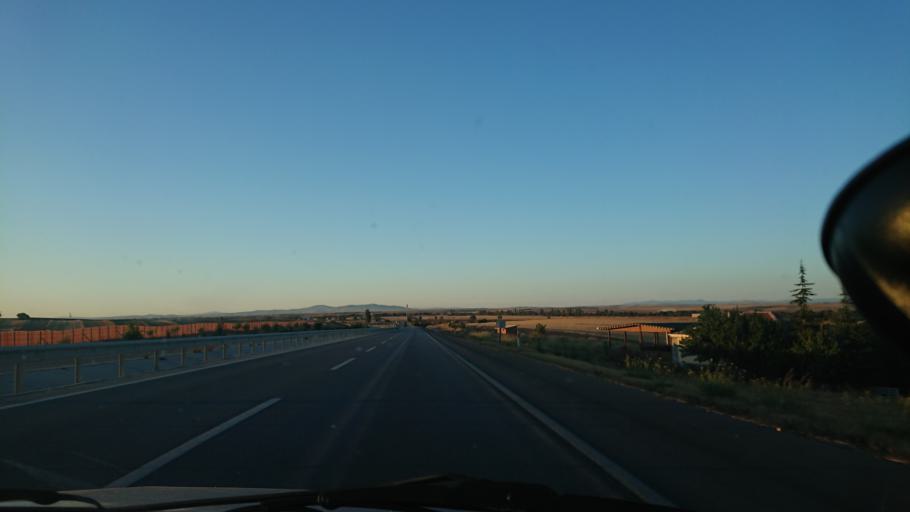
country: TR
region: Eskisehir
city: Mahmudiye
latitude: 39.5124
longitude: 30.9642
